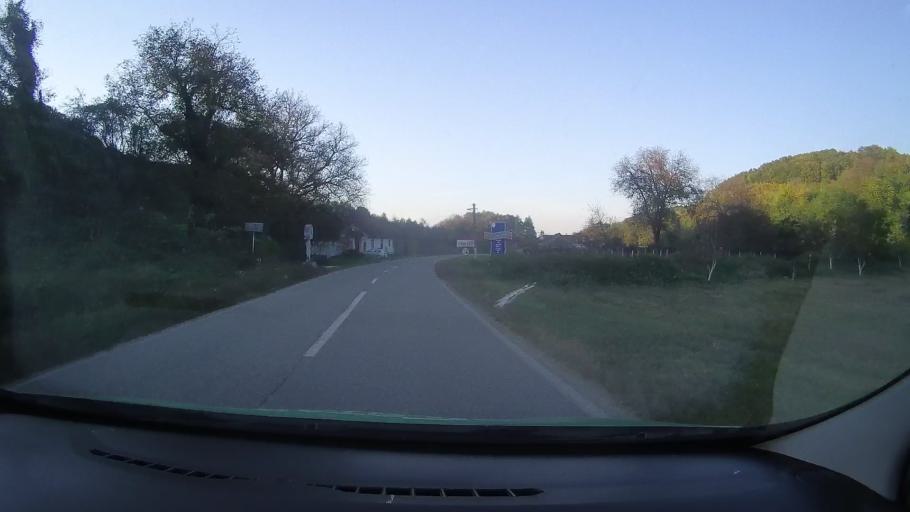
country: RO
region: Timis
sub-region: Comuna Fardea
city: Fardea
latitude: 45.7079
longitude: 22.1601
